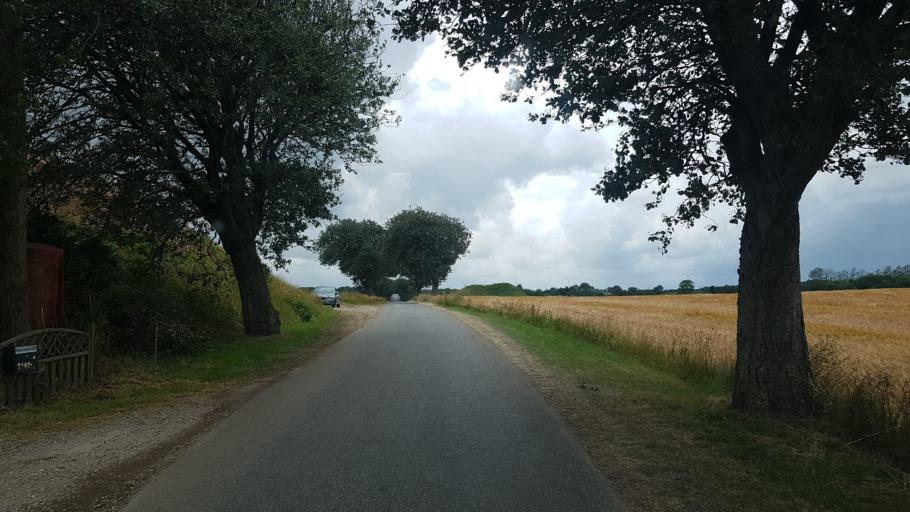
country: DK
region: South Denmark
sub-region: Kolding Kommune
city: Lunderskov
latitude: 55.5047
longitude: 9.3174
